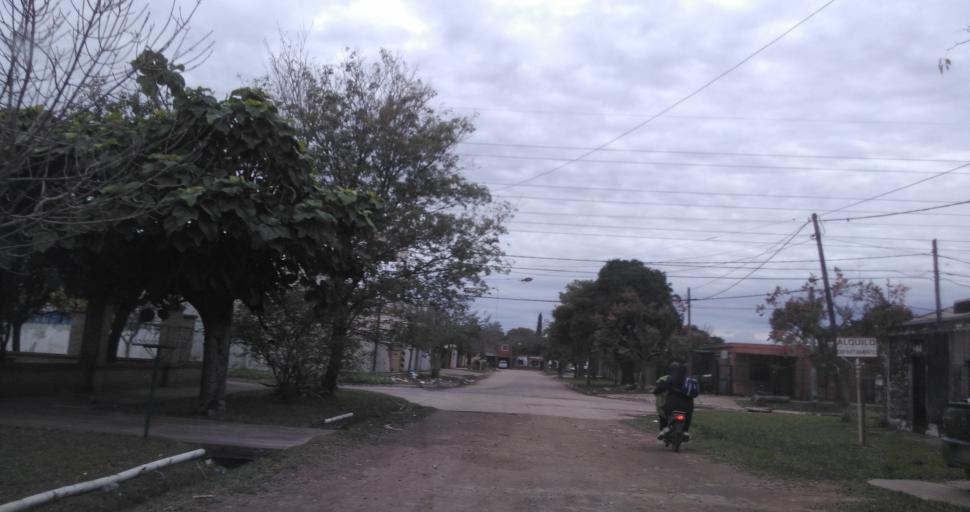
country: AR
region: Chaco
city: Resistencia
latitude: -27.4708
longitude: -58.9661
